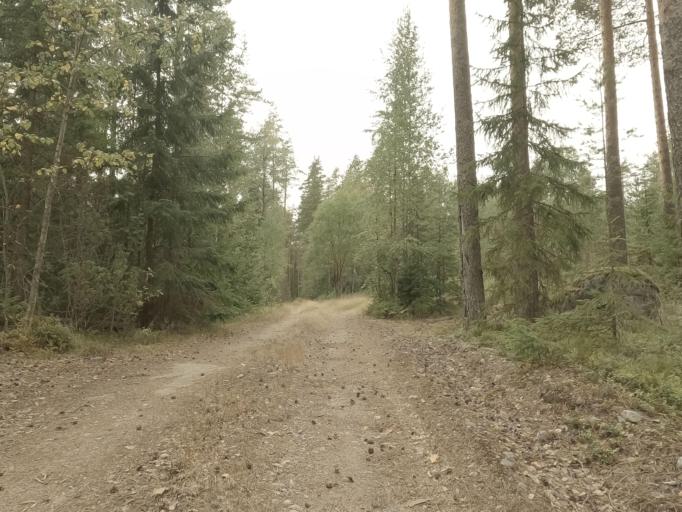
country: RU
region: Leningrad
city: Kamennogorsk
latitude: 61.0202
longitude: 29.1849
